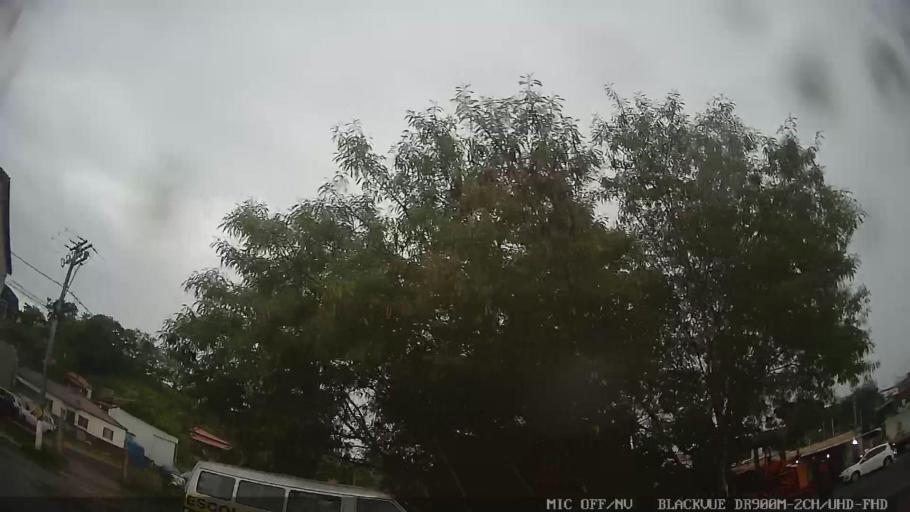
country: BR
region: Sao Paulo
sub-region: Pedreira
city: Pedreira
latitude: -22.7356
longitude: -46.9006
